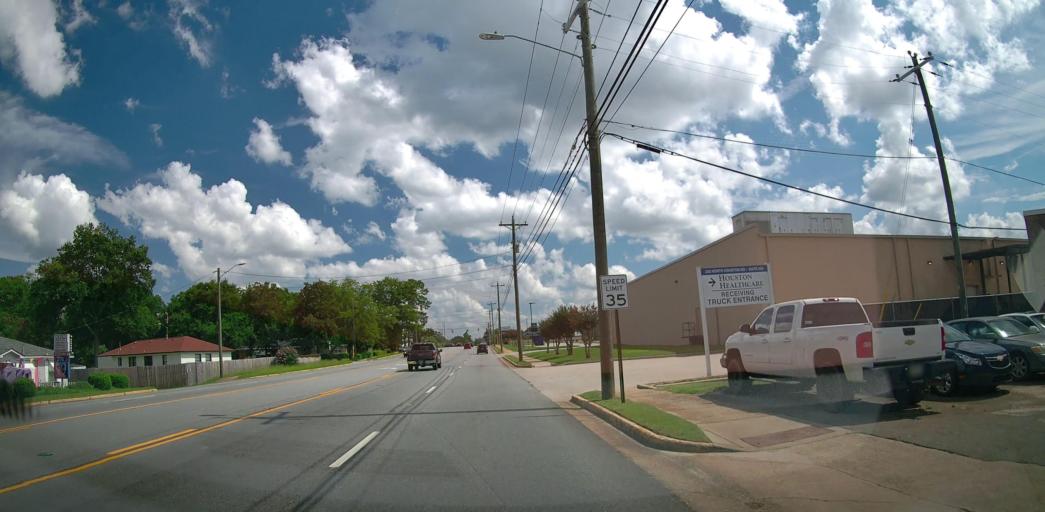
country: US
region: Georgia
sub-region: Houston County
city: Warner Robins
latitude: 32.6224
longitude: -83.6416
